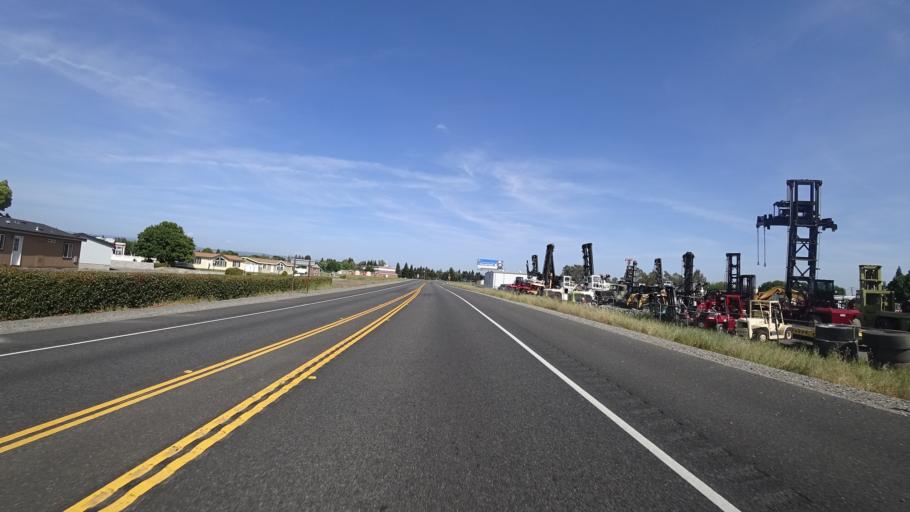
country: US
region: California
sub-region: Butte County
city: Chico
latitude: 39.7925
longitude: -121.8968
